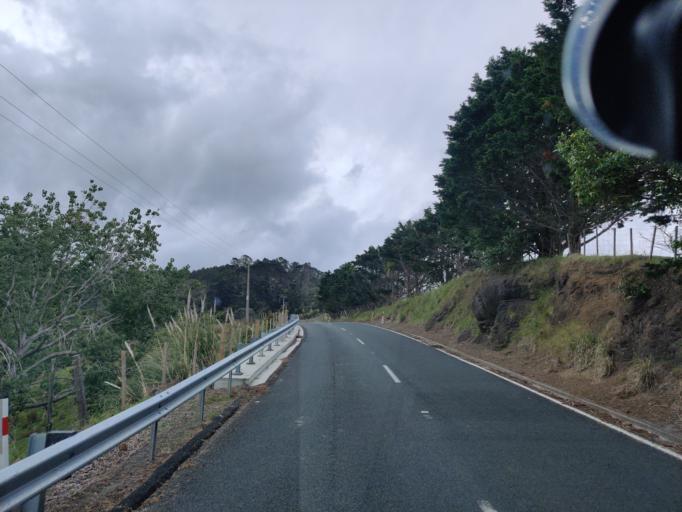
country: NZ
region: Auckland
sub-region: Auckland
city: Warkworth
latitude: -36.2808
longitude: 174.7864
